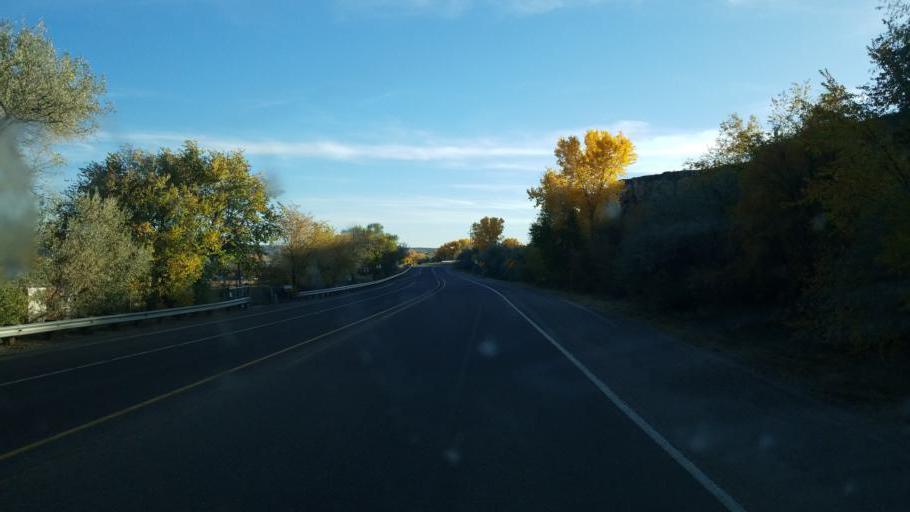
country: US
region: New Mexico
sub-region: San Juan County
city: Bloomfield
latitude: 36.7182
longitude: -107.8353
